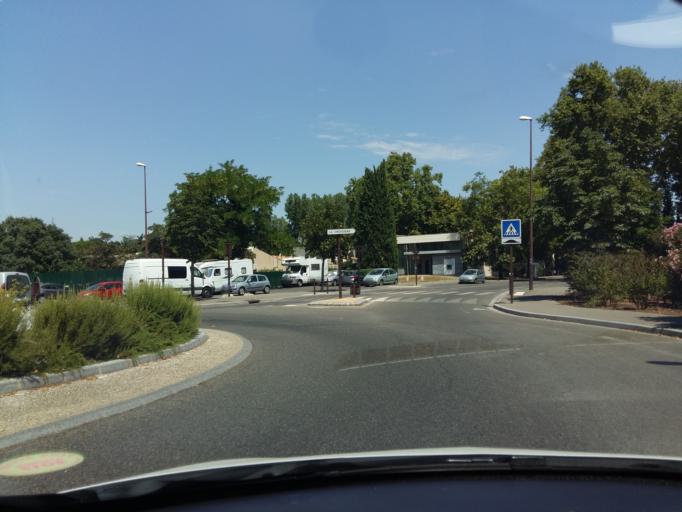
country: FR
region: Provence-Alpes-Cote d'Azur
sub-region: Departement du Vaucluse
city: Avignon
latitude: 43.9470
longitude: 4.8289
